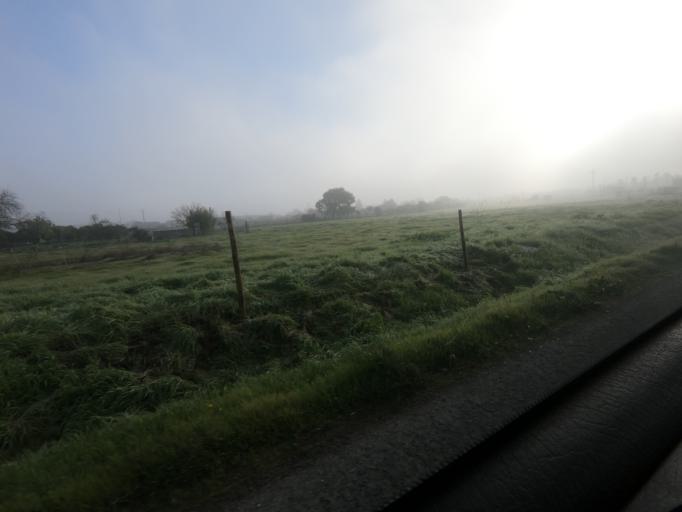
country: PT
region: Setubal
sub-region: Palmela
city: Pinhal Novo
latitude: 38.6054
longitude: -8.9064
